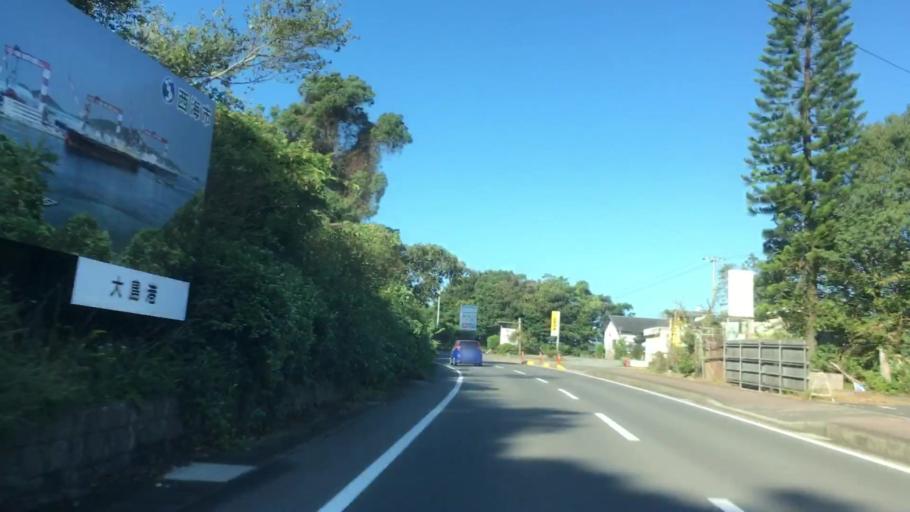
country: JP
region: Nagasaki
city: Sasebo
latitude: 33.0404
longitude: 129.6528
